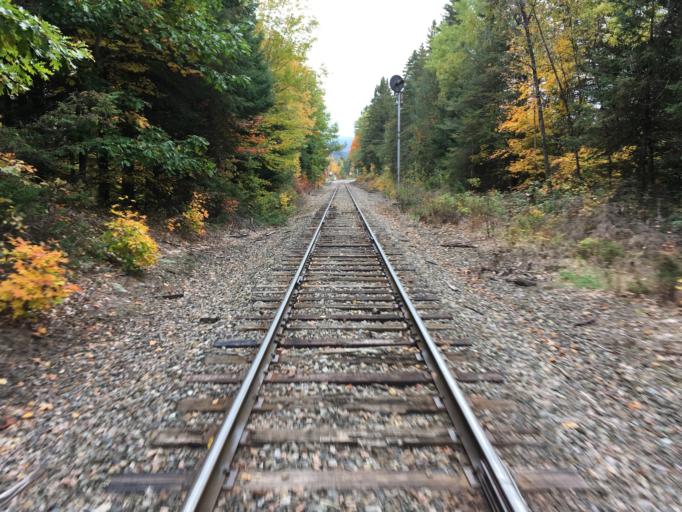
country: US
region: Vermont
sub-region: Caledonia County
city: Lyndonville
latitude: 44.6327
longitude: -71.9756
